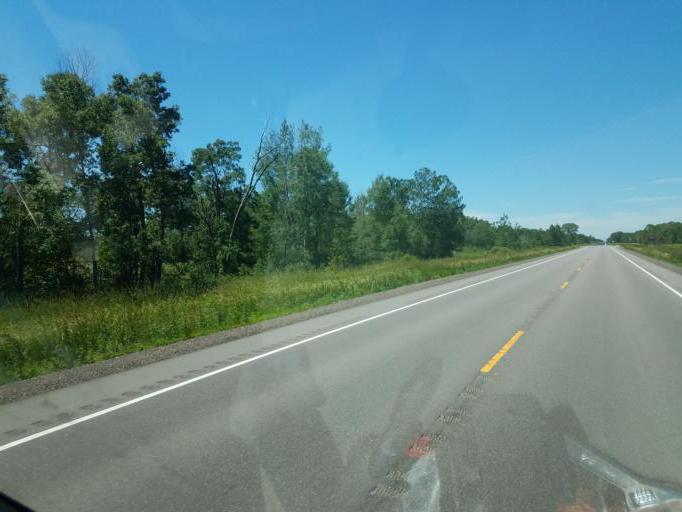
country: US
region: Wisconsin
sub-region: Juneau County
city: New Lisbon
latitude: 44.0246
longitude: -90.1521
